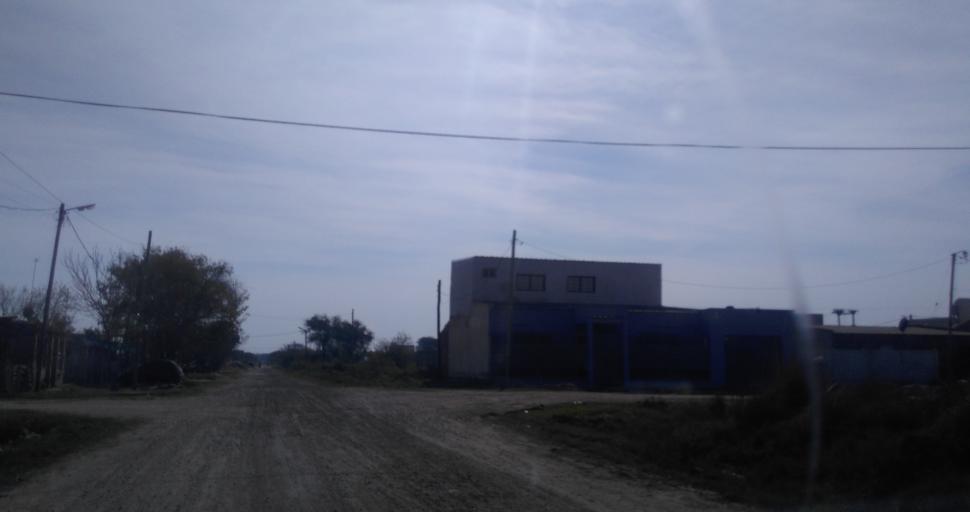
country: AR
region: Chaco
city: Fontana
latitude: -27.4602
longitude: -59.0429
